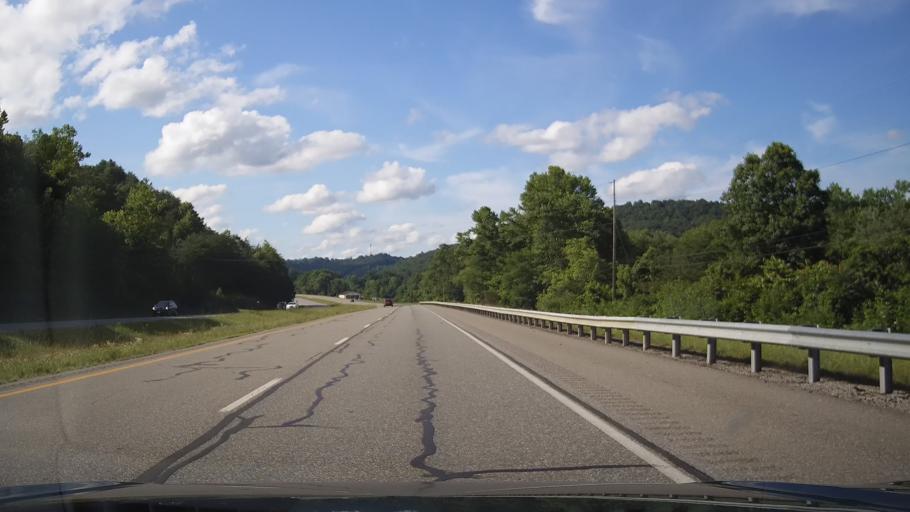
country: US
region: Kentucky
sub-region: Lawrence County
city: Louisa
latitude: 38.1477
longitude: -82.6394
